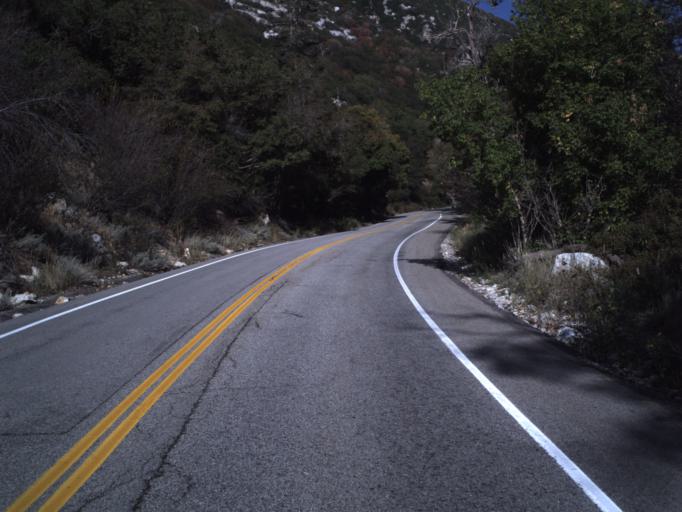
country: US
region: Utah
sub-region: Salt Lake County
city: Granite
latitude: 40.5717
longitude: -111.7495
